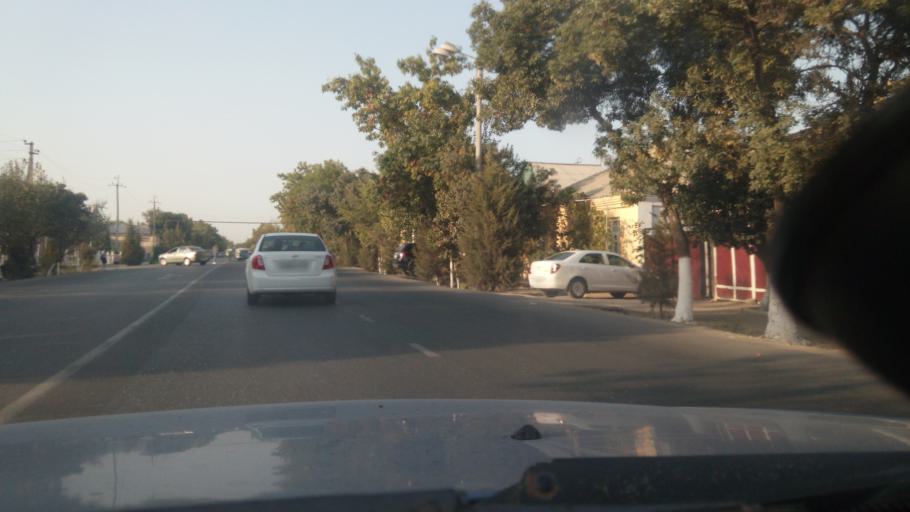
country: UZ
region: Sirdaryo
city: Guliston
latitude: 40.4810
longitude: 68.7767
